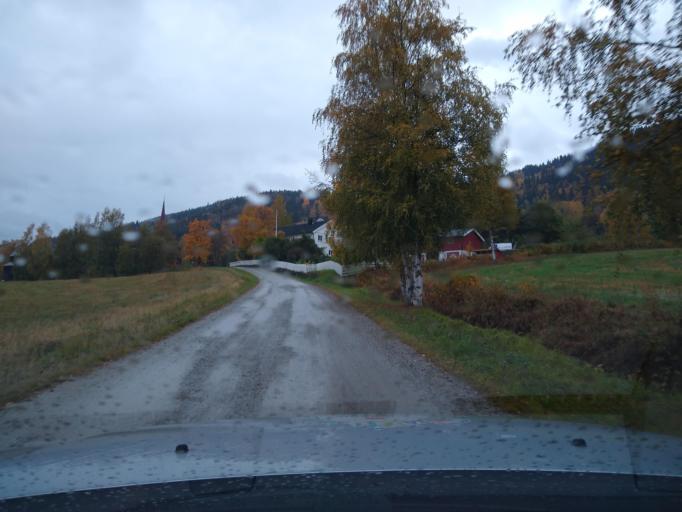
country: NO
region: Oppland
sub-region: Ringebu
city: Ringebu
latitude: 61.5069
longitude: 10.1725
